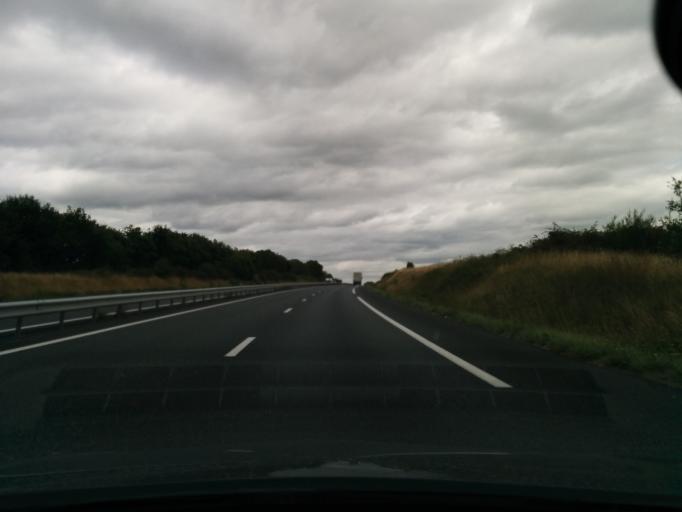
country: FR
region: Centre
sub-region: Departement de l'Indre
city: Chantome
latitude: 46.4698
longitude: 1.4965
